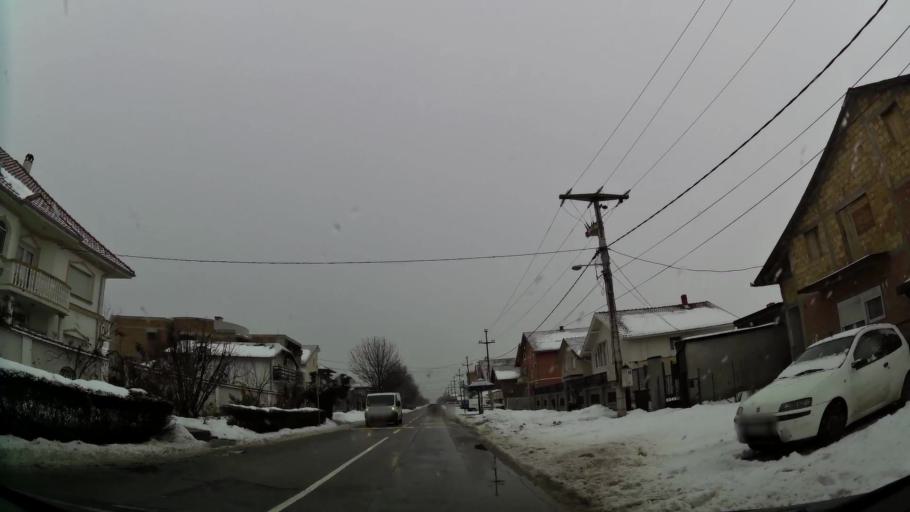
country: RS
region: Central Serbia
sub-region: Belgrade
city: Zemun
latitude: 44.8494
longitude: 20.3398
